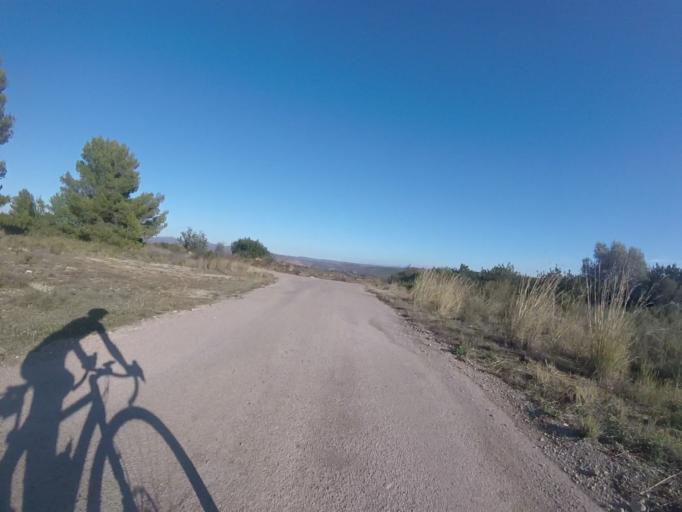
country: ES
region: Valencia
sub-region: Provincia de Castello
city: Cuevas de Vinroma
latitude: 40.2899
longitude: 0.0855
